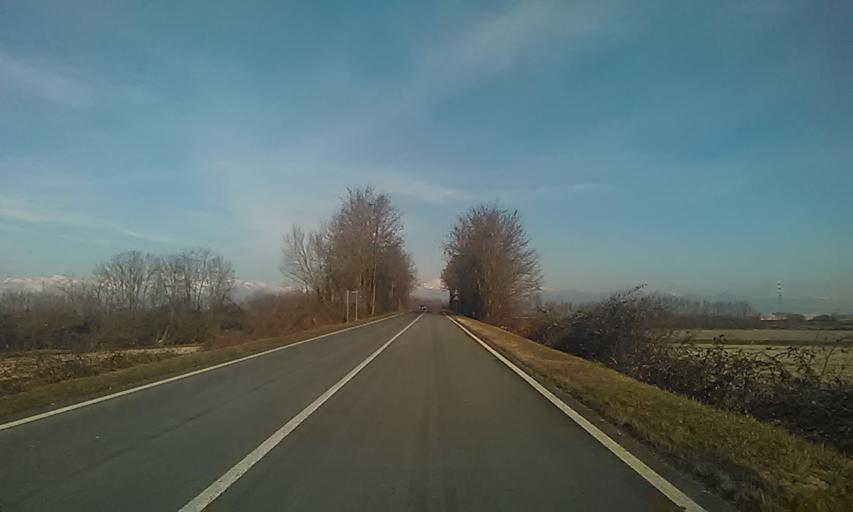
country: IT
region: Piedmont
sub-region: Provincia di Vercelli
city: Formigliana
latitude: 45.4387
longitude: 8.2931
